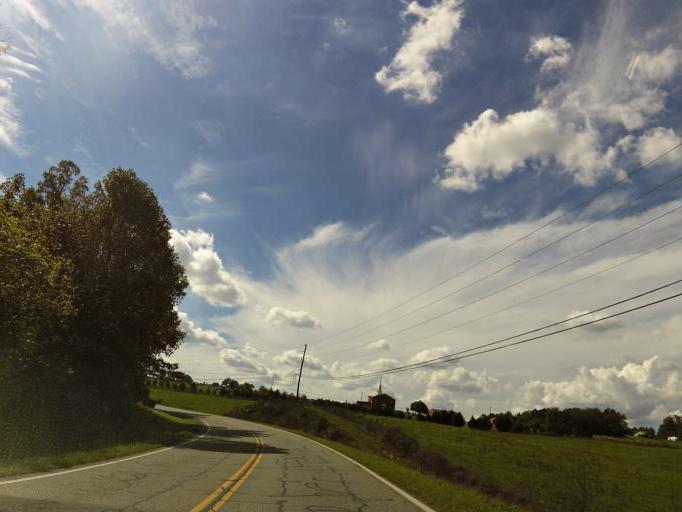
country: US
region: Georgia
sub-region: Pickens County
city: Nelson
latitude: 34.4133
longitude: -84.4153
